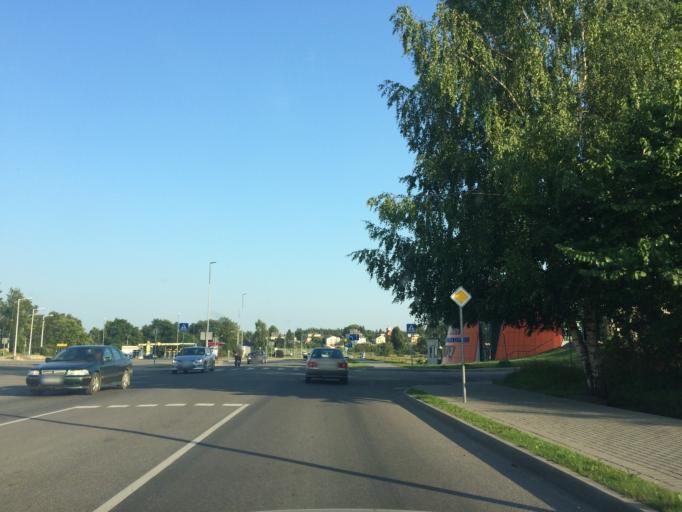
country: LV
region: Rezekne
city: Rezekne
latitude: 56.5168
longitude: 27.3505
